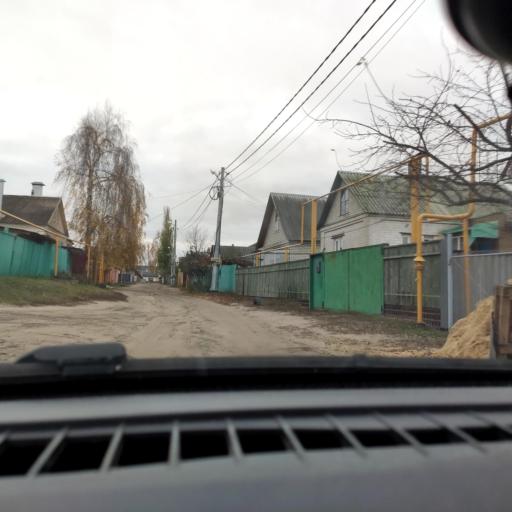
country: RU
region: Voronezj
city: Podgornoye
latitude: 51.7339
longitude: 39.1420
